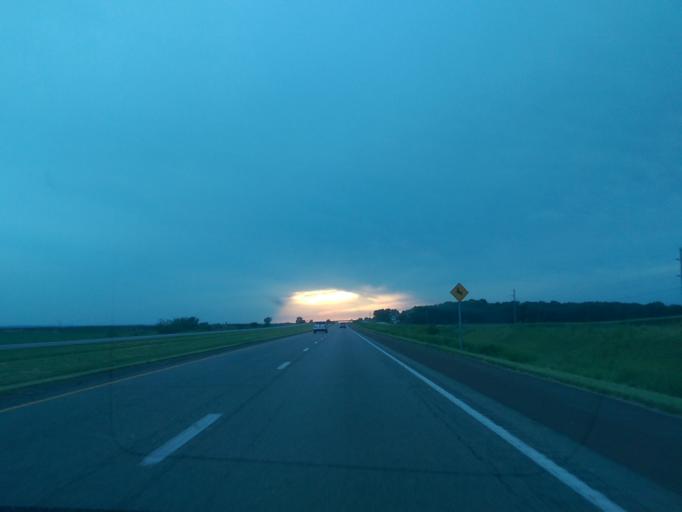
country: US
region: Missouri
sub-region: Holt County
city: Mound City
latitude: 40.1539
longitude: -95.2578
